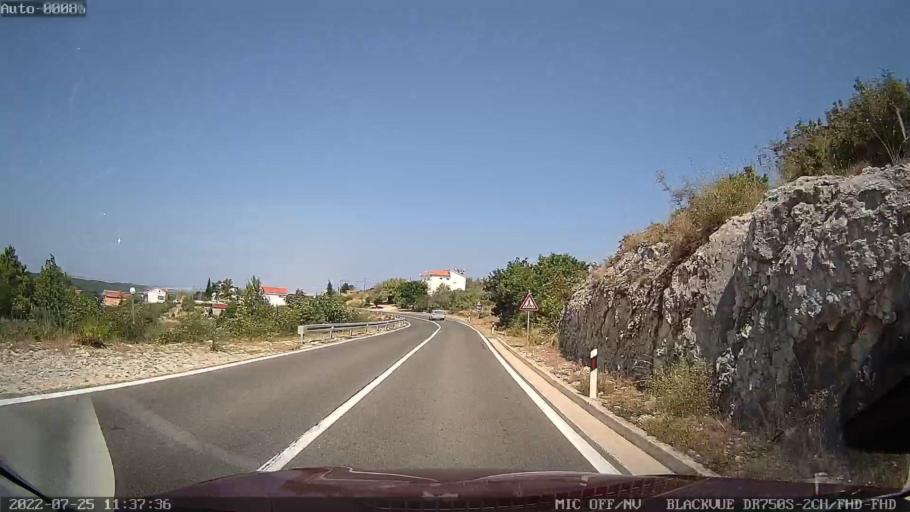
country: HR
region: Zadarska
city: Razanac
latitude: 44.2478
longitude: 15.3886
